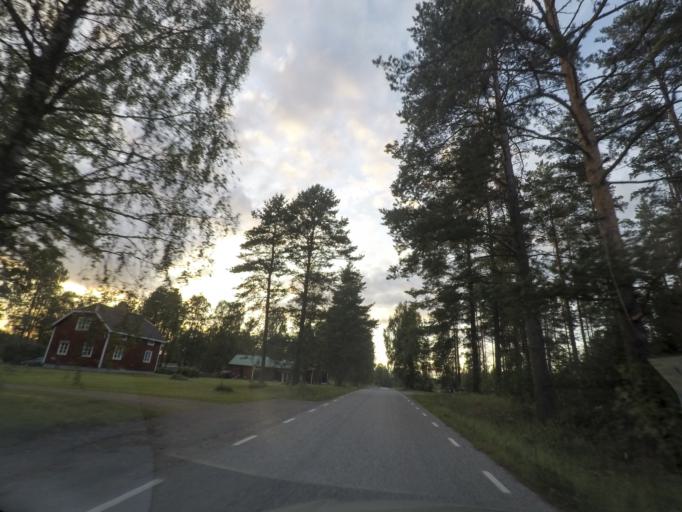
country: SE
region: OErebro
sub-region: Hallefors Kommun
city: Haellefors
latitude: 59.9104
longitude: 14.5483
